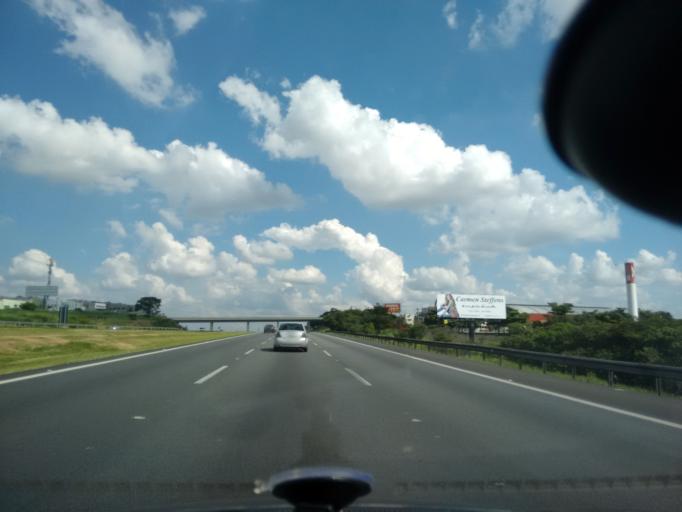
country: BR
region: Sao Paulo
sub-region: Campinas
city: Campinas
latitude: -22.9840
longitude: -47.1118
